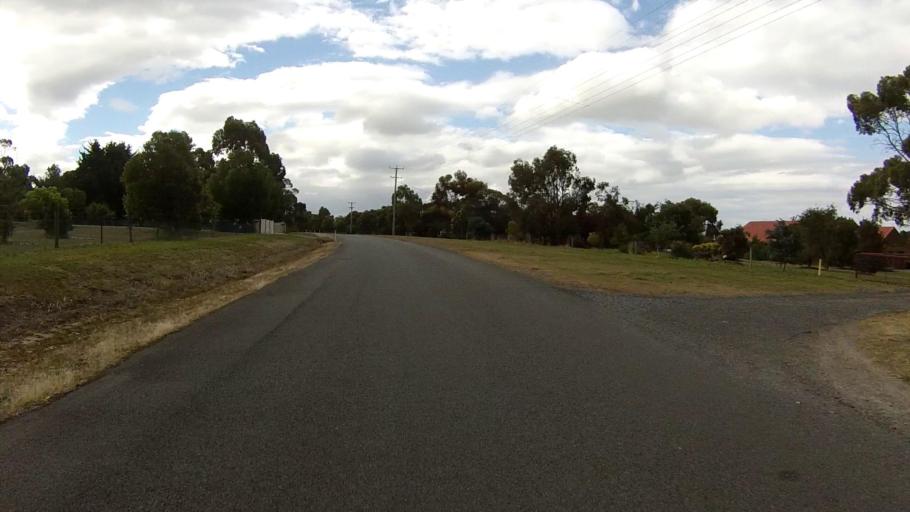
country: AU
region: Tasmania
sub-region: Clarence
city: Acton Park
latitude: -42.8625
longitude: 147.4866
